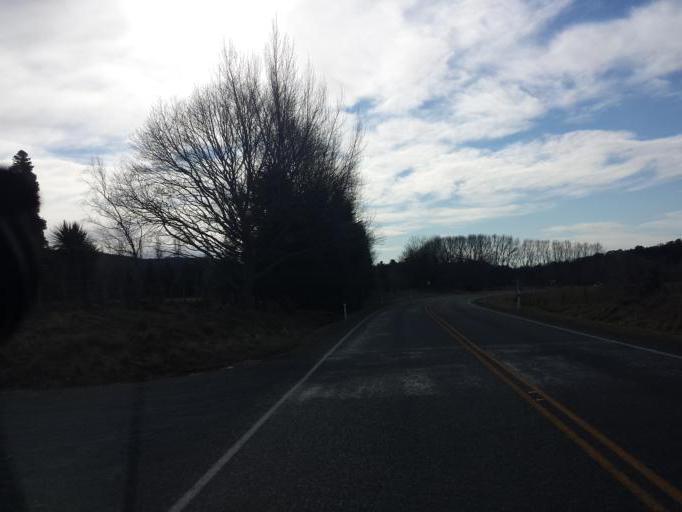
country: NZ
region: Canterbury
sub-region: Timaru District
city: Pleasant Point
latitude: -44.1135
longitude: 171.1345
